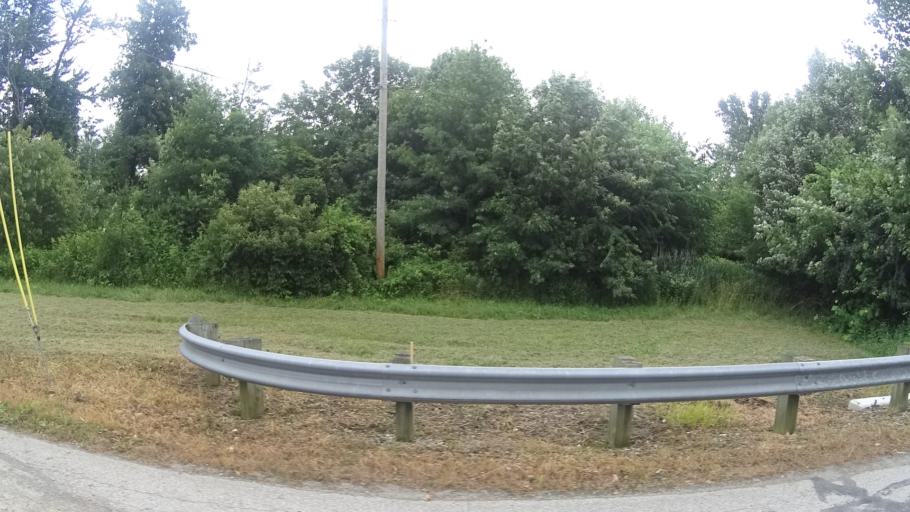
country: US
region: Ohio
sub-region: Huron County
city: Wakeman
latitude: 41.3275
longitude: -82.4386
